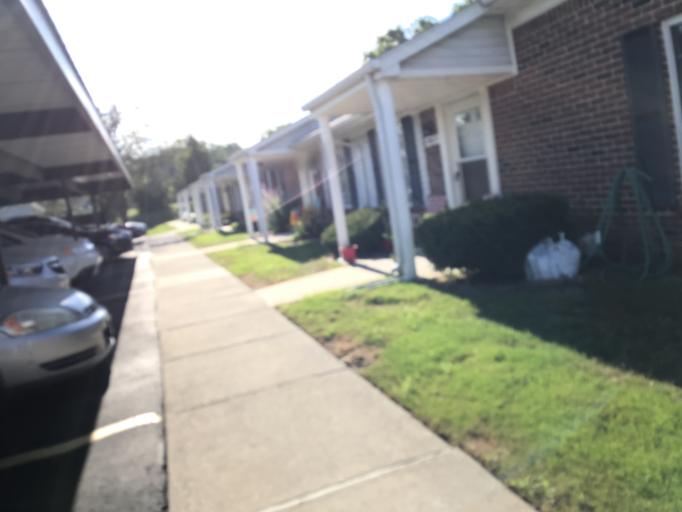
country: US
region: Michigan
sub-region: Oakland County
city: Farmington Hills
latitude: 42.4823
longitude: -83.3400
